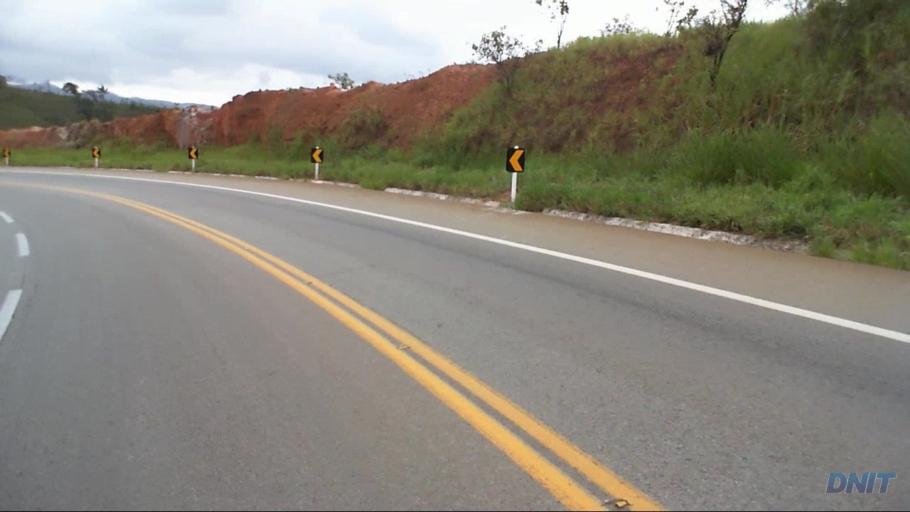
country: BR
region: Minas Gerais
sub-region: Nova Era
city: Nova Era
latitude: -19.7947
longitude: -43.0531
